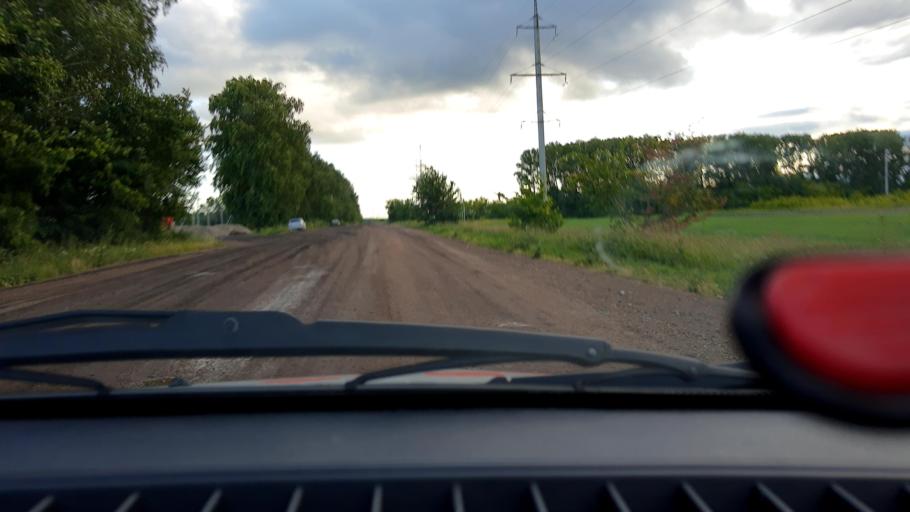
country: RU
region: Bashkortostan
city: Tolbazy
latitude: 54.1951
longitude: 55.8851
